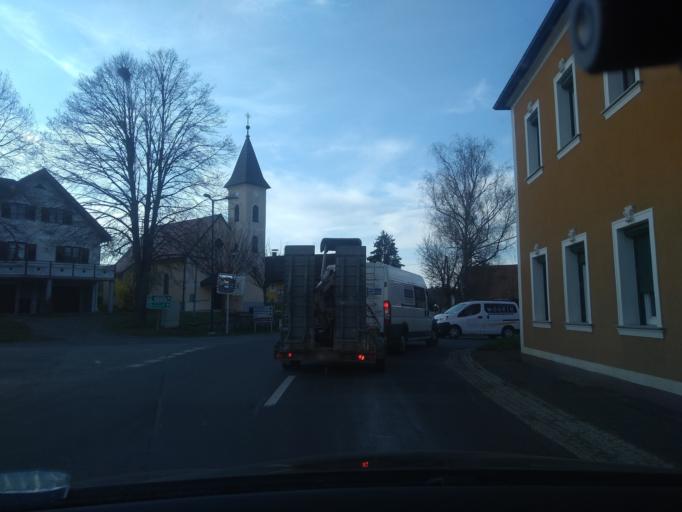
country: AT
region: Styria
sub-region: Politischer Bezirk Suedoststeiermark
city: Sankt Peter am Ottersbach
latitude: 46.7793
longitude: 15.7665
